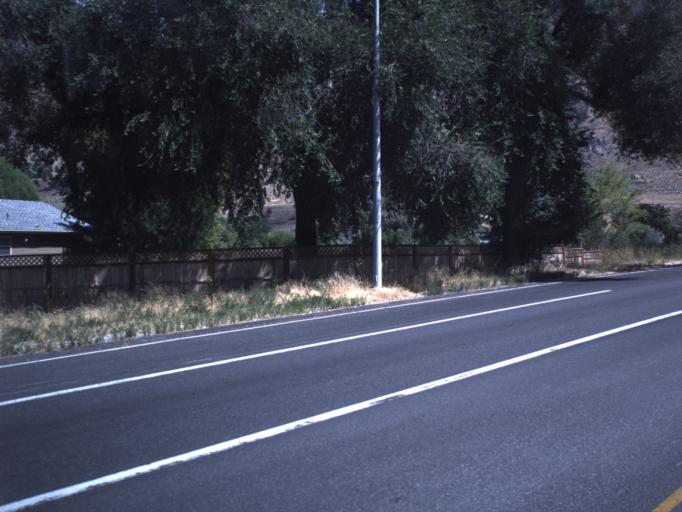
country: US
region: Utah
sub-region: Box Elder County
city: Brigham City
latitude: 41.5297
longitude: -112.0206
